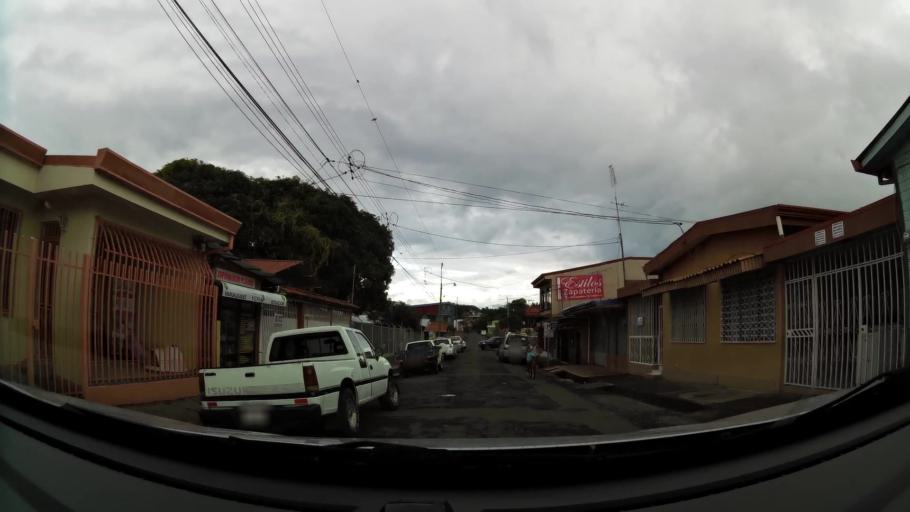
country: CR
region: Puntarenas
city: Esparza
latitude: 9.9920
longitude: -84.6674
